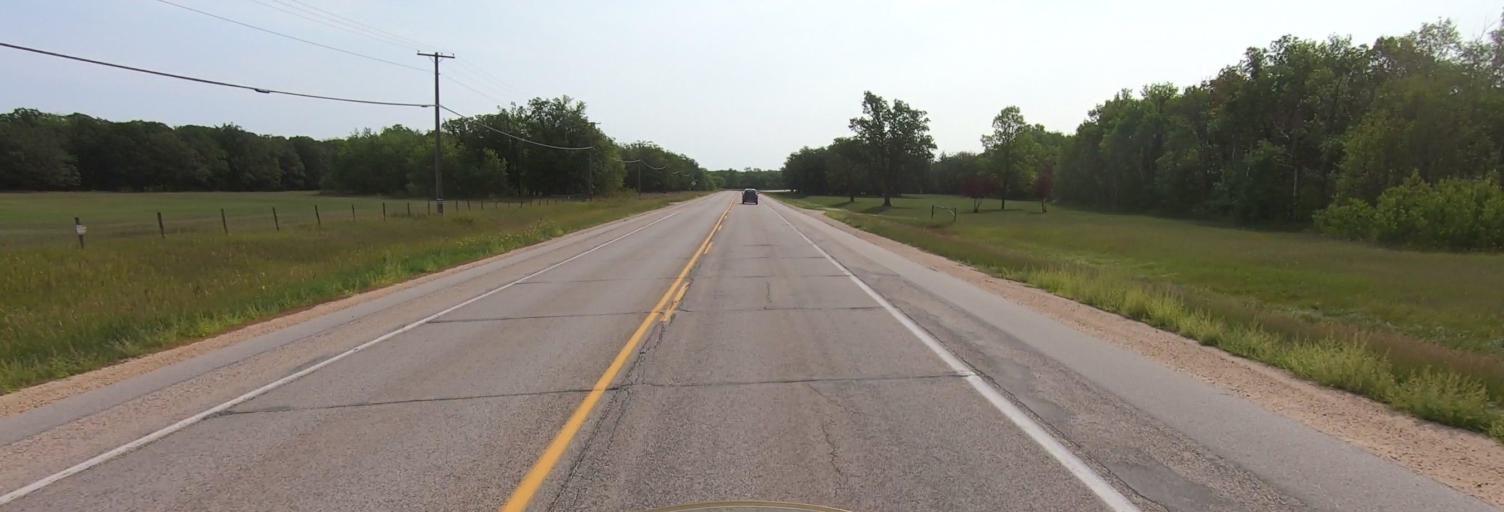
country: CA
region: Manitoba
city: Niverville
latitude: 49.7365
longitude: -97.1123
